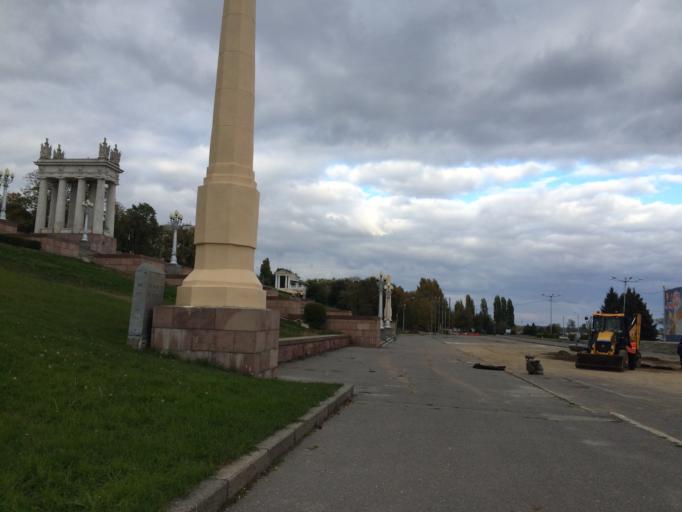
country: RU
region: Volgograd
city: Volgograd
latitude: 48.7033
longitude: 44.5211
